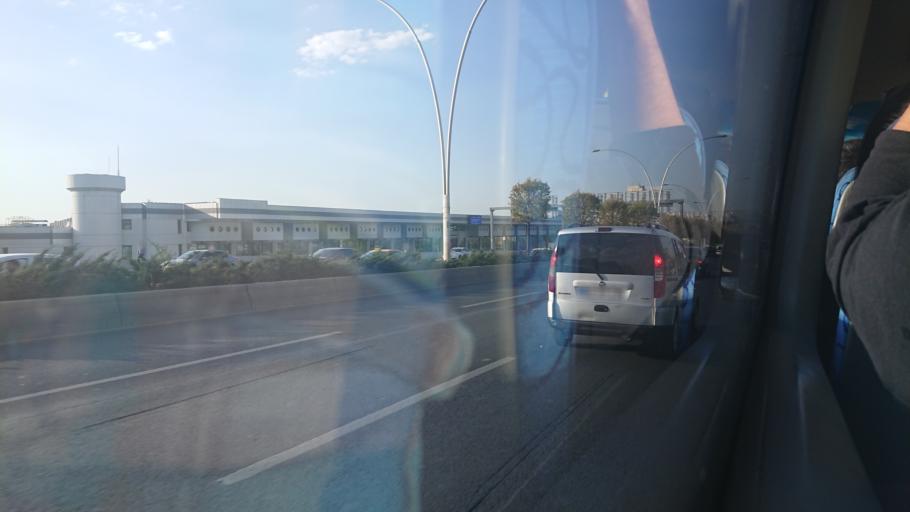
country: TR
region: Ankara
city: Ankara
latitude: 39.9165
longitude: 32.8146
